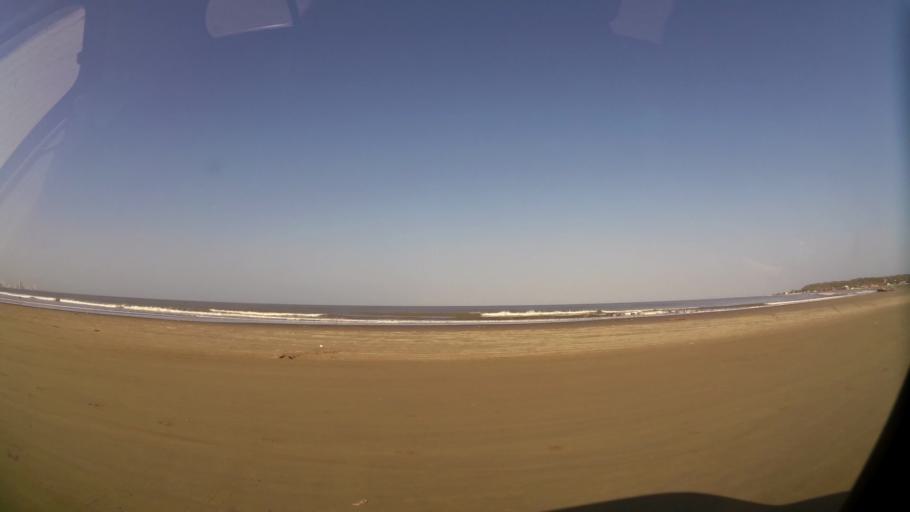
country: CO
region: Bolivar
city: Cartagena
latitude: 10.4883
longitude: -75.4920
